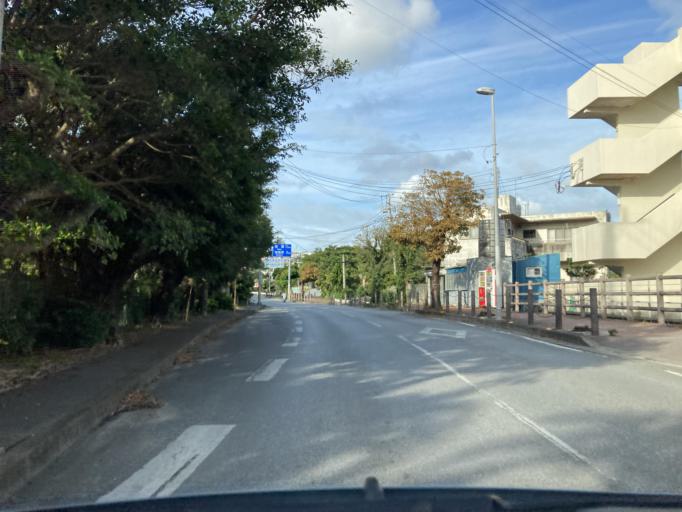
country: JP
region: Okinawa
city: Tomigusuku
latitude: 26.1410
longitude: 127.7476
